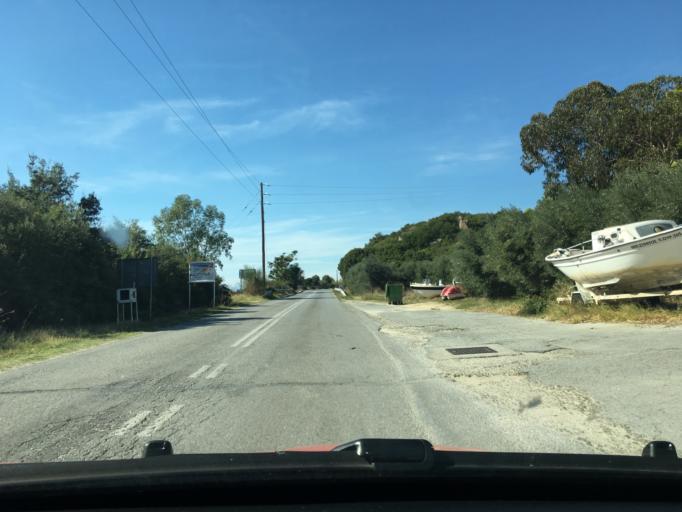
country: GR
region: Central Macedonia
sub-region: Nomos Chalkidikis
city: Ouranoupolis
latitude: 40.3326
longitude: 23.9753
